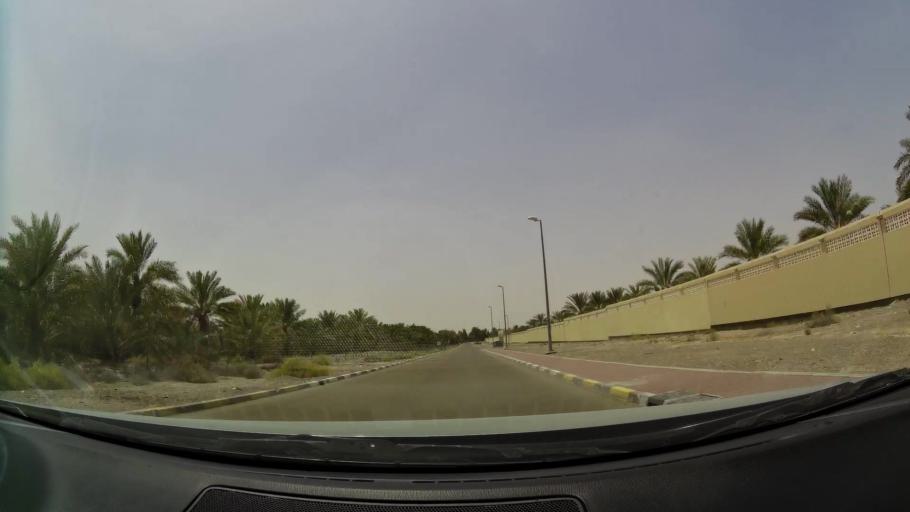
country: AE
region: Abu Dhabi
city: Al Ain
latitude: 24.2005
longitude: 55.7046
